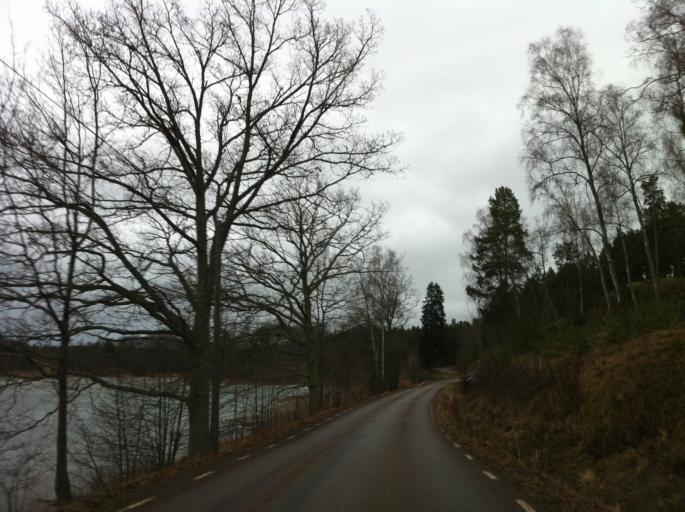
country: SE
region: Kalmar
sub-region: Vasterviks Kommun
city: Vaestervik
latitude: 57.9069
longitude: 16.6976
